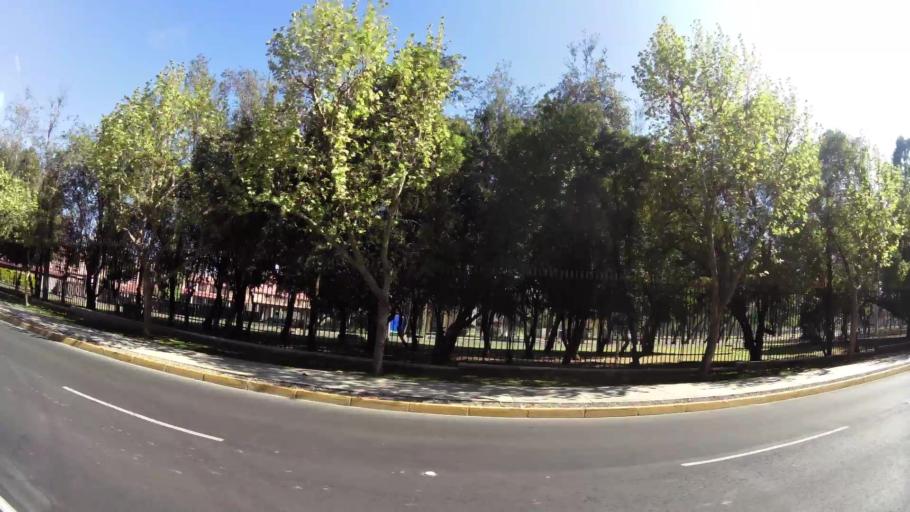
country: CL
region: Santiago Metropolitan
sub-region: Provincia de Santiago
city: Villa Presidente Frei, Nunoa, Santiago, Chile
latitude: -33.4116
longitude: -70.5806
